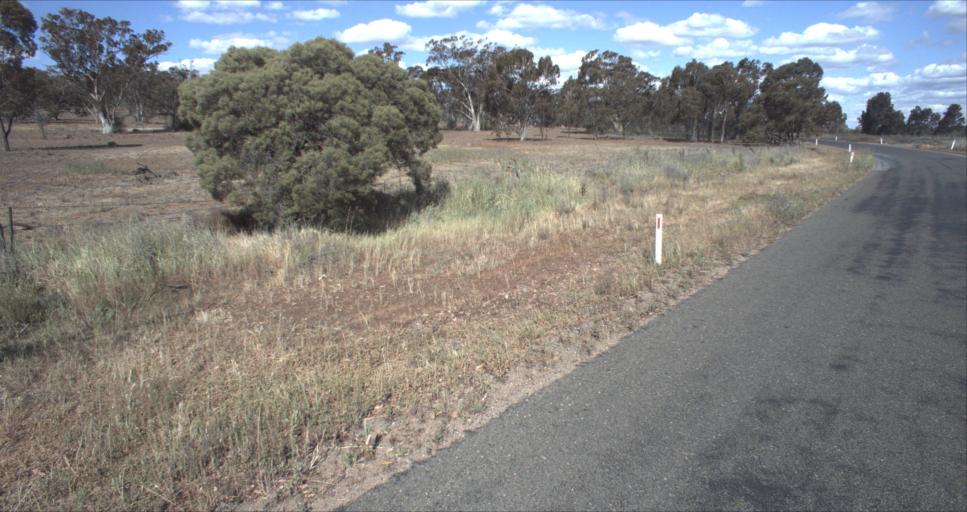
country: AU
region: New South Wales
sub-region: Griffith
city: Griffith
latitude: -34.4125
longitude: 146.2183
